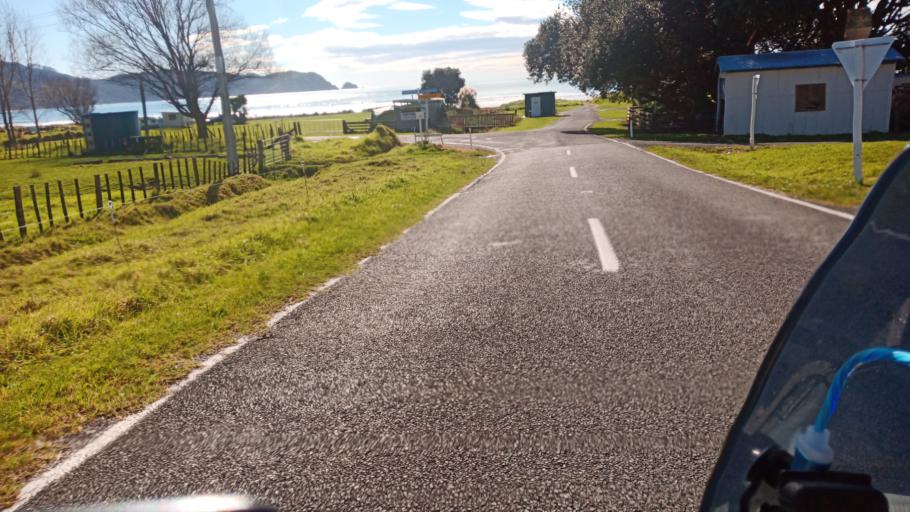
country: NZ
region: Gisborne
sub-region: Gisborne District
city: Gisborne
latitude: -38.2478
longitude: 178.3157
